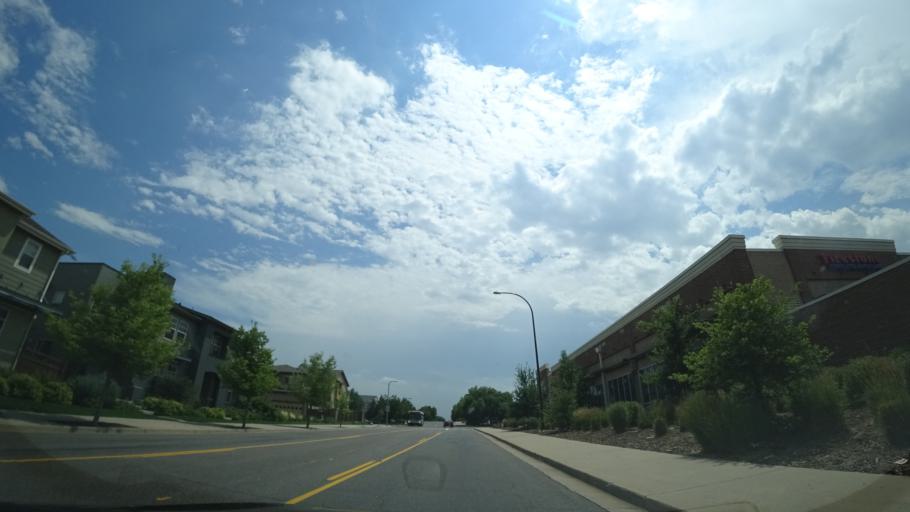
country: US
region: Colorado
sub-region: Jefferson County
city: Lakewood
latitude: 39.7062
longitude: -105.0798
